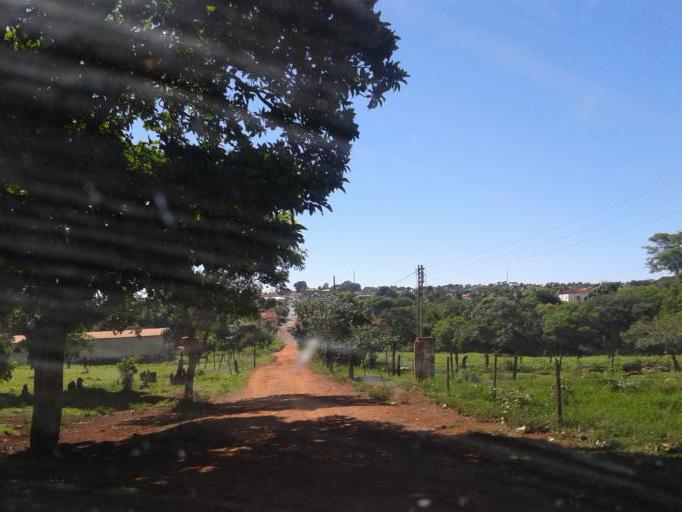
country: BR
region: Minas Gerais
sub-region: Capinopolis
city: Capinopolis
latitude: -18.6793
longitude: -49.5779
